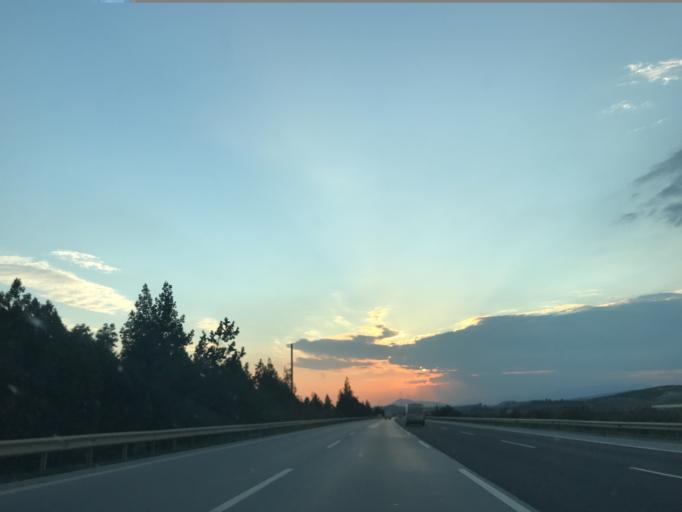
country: TR
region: Mersin
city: Yenice
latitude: 37.0121
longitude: 34.9907
